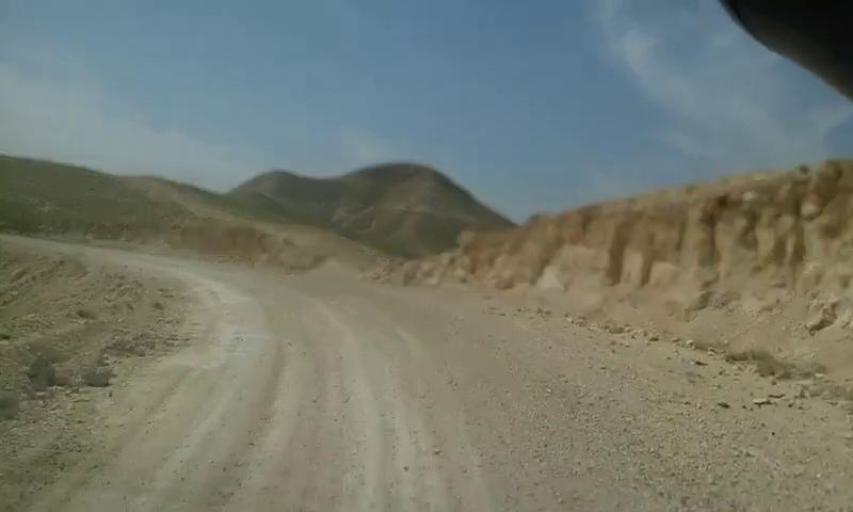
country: PS
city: `Arab ar Rashaydah
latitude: 31.5020
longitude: 35.2944
